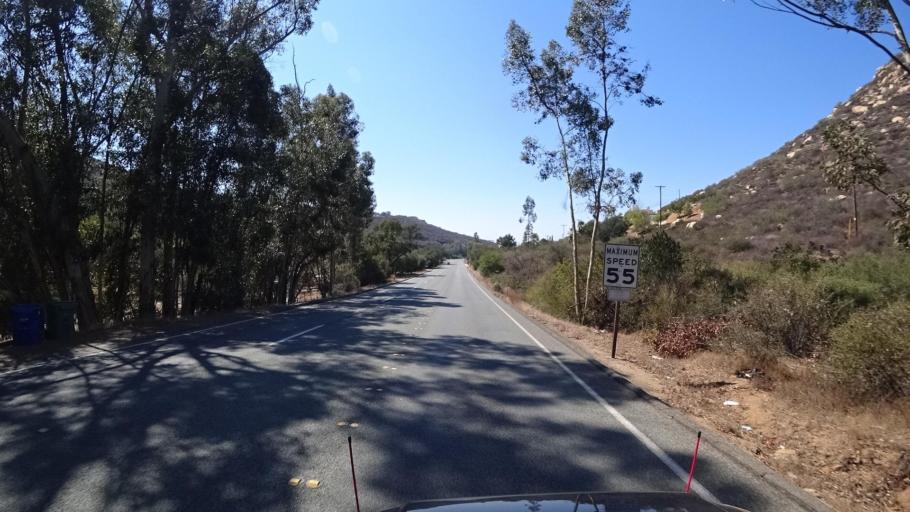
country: US
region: California
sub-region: San Diego County
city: Crest
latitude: 32.8098
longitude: -116.8809
